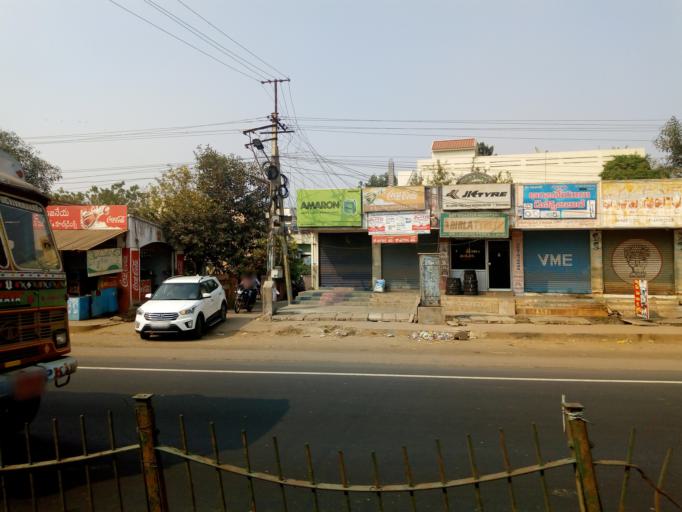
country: IN
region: Andhra Pradesh
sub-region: West Godavari
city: Eluru
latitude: 16.6340
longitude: 80.9633
